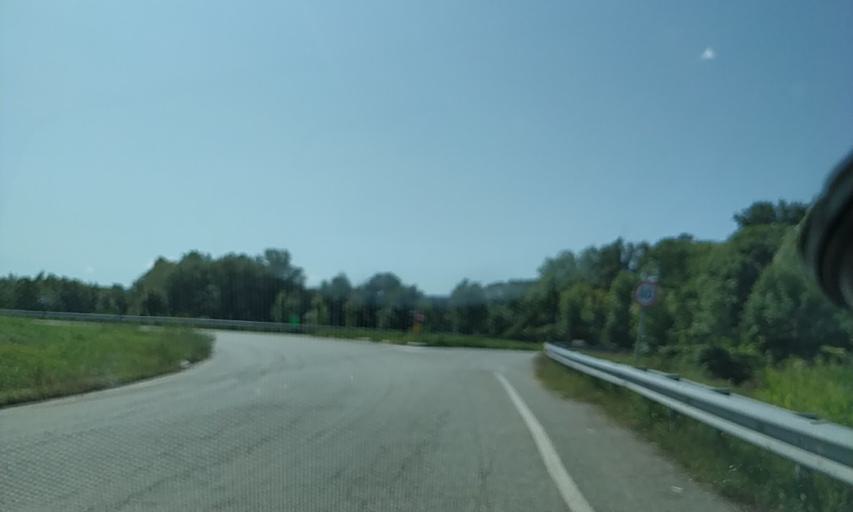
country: IT
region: Piedmont
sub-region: Provincia di Biella
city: Ponderano
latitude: 45.5255
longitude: 8.0478
